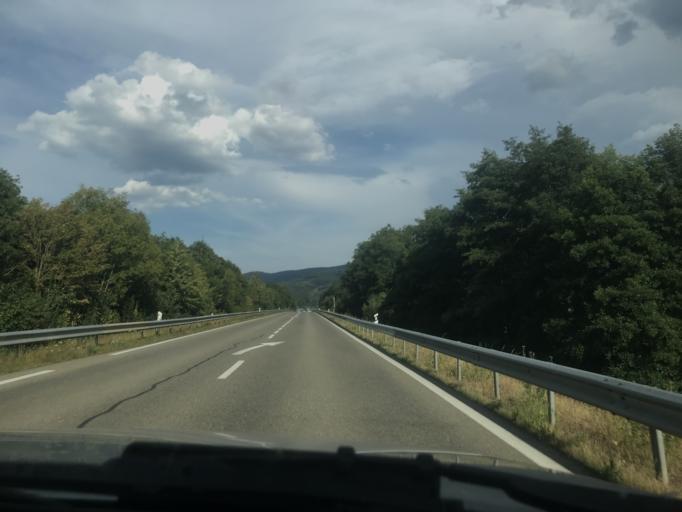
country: FR
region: Lorraine
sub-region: Departement des Vosges
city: Ban-de-Laveline
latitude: 48.2912
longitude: 7.0962
